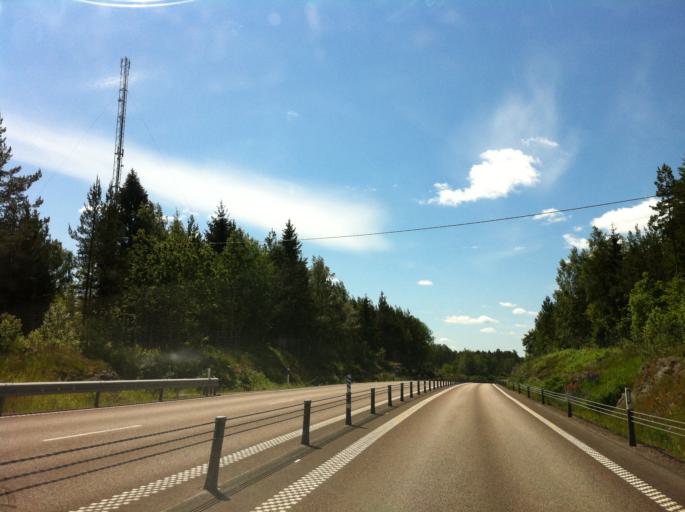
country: SE
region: Vaestra Goetaland
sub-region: Melleruds Kommun
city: Mellerud
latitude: 58.8025
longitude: 12.5264
